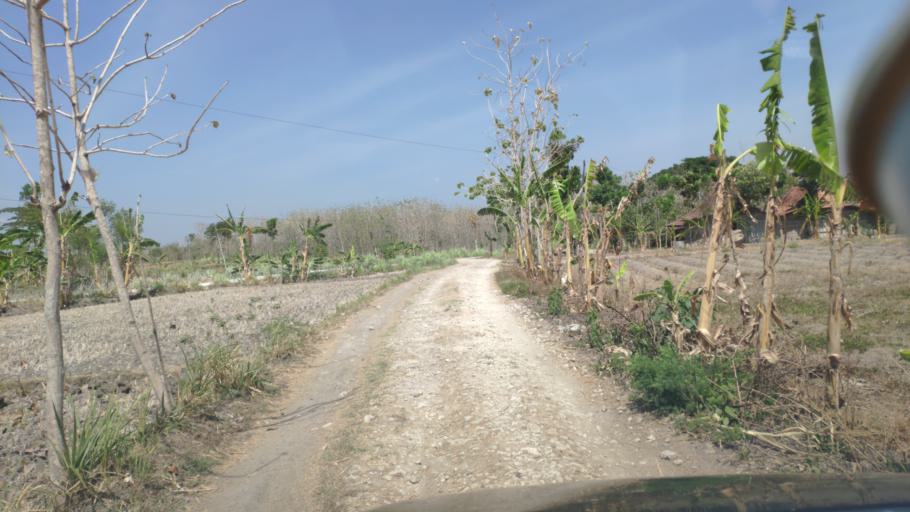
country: ID
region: Central Java
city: Sendanggayam
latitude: -7.0395
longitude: 111.3509
